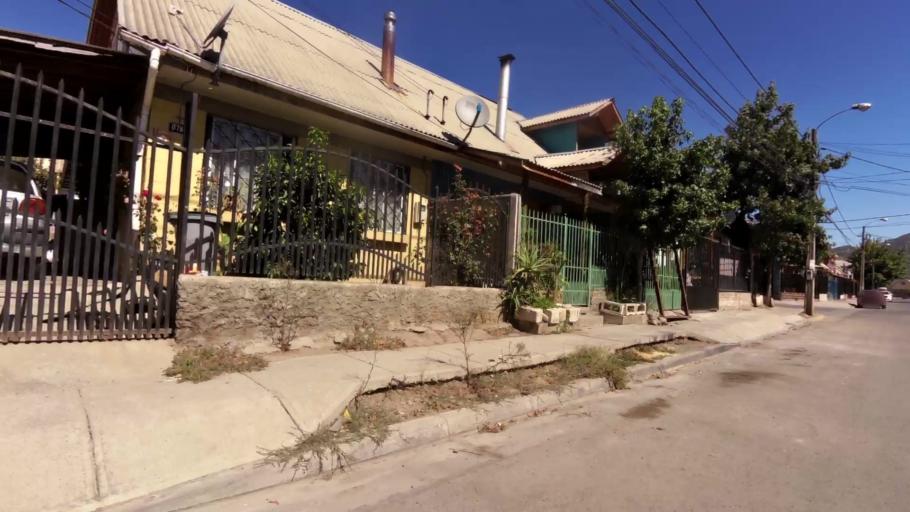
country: CL
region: O'Higgins
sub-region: Provincia de Colchagua
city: Chimbarongo
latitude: -34.5933
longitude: -71.0004
